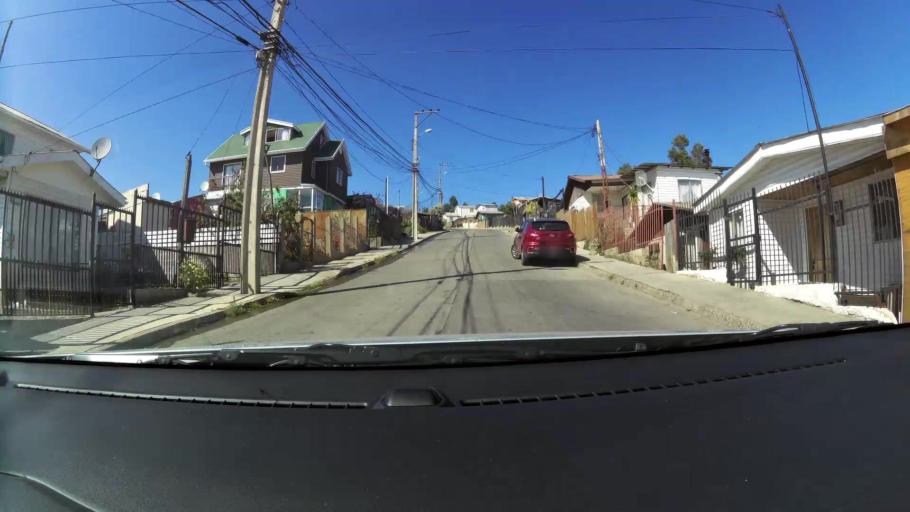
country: CL
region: Valparaiso
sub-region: Provincia de Valparaiso
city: Valparaiso
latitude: -33.0518
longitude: -71.6435
